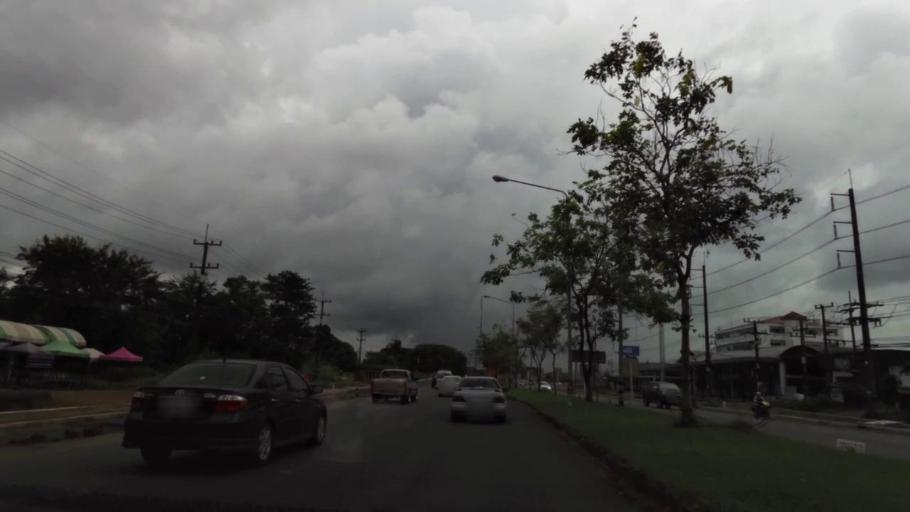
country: TH
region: Chanthaburi
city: Chanthaburi
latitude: 12.6145
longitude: 102.1393
